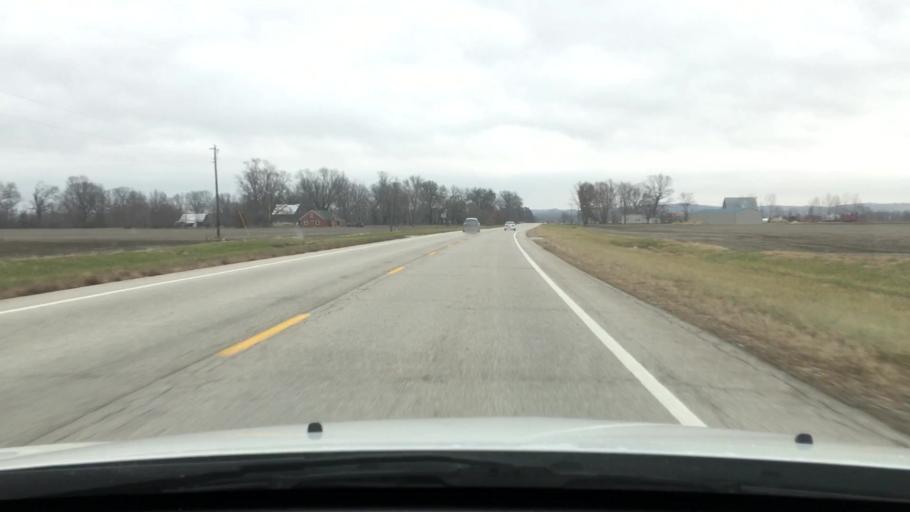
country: US
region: Missouri
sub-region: Pike County
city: Louisiana
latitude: 39.4848
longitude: -91.0140
